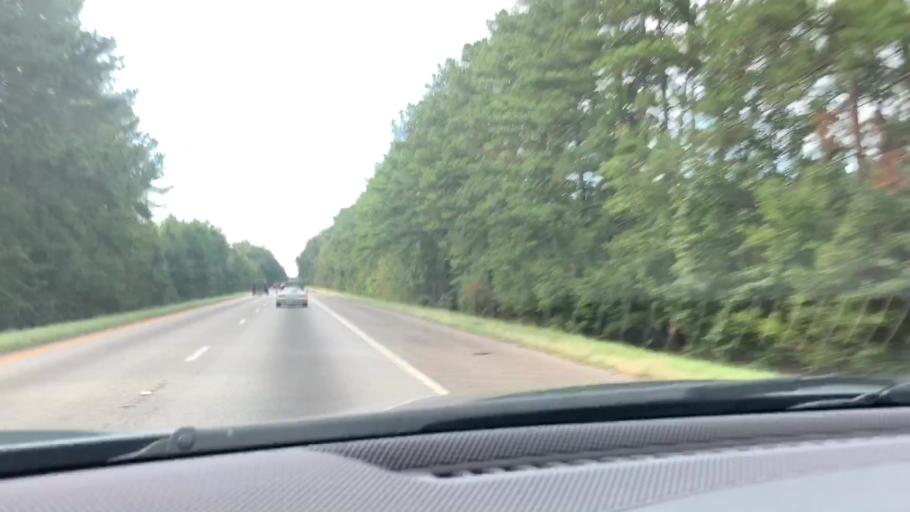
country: US
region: South Carolina
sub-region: Dorchester County
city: Saint George
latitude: 33.3403
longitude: -80.5706
